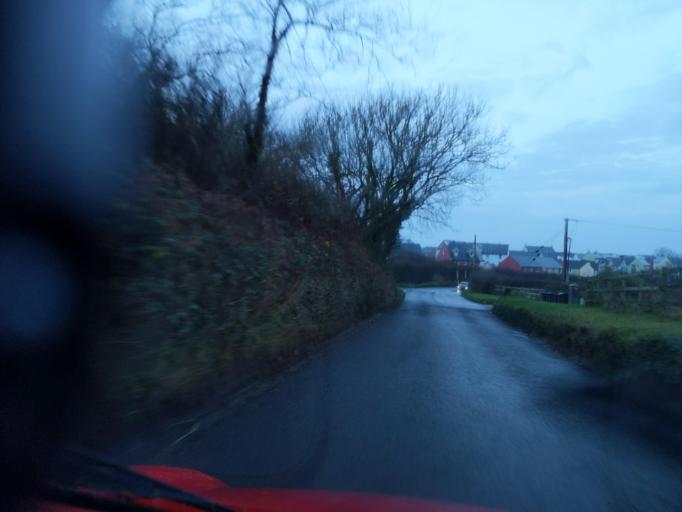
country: GB
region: England
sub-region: Plymouth
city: Plymstock
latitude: 50.3479
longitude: -4.0778
